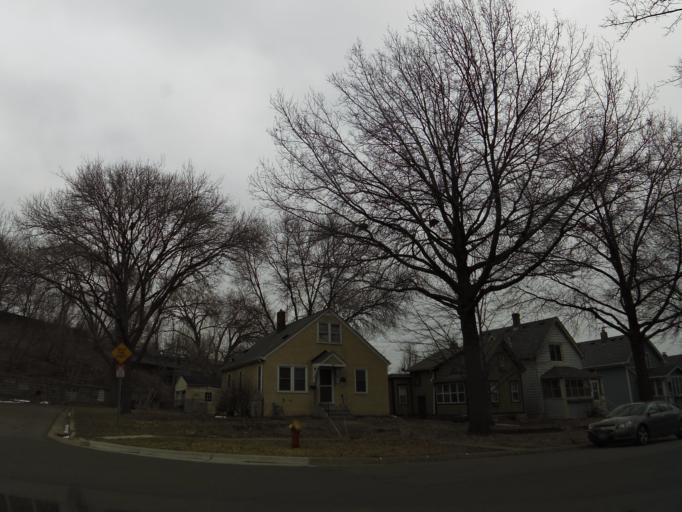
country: US
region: Minnesota
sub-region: Dakota County
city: West Saint Paul
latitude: 44.9296
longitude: -93.1415
